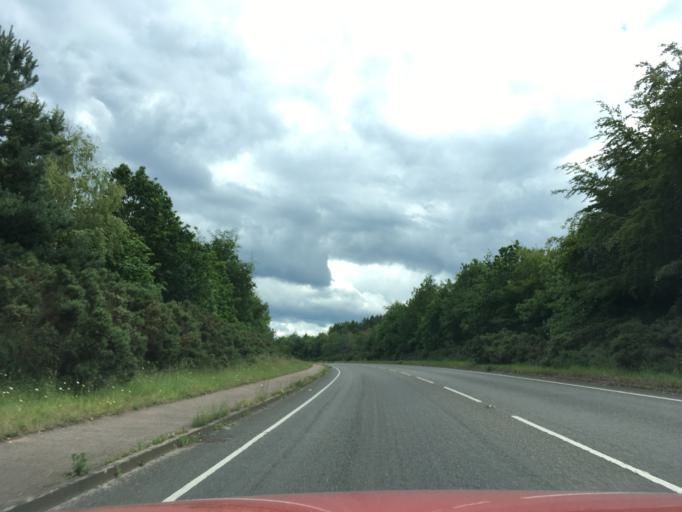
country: GB
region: England
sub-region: Central Bedfordshire
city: Aspley Guise
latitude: 52.0037
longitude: -0.6435
